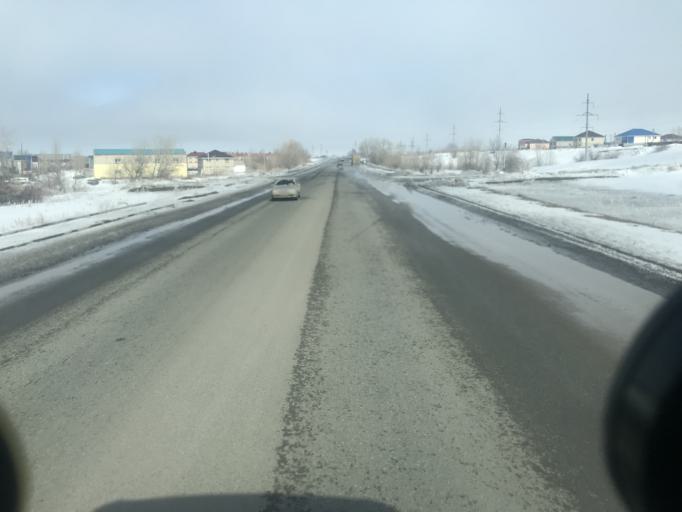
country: KZ
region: Aqtoebe
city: Aqtobe
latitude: 50.2834
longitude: 57.2835
